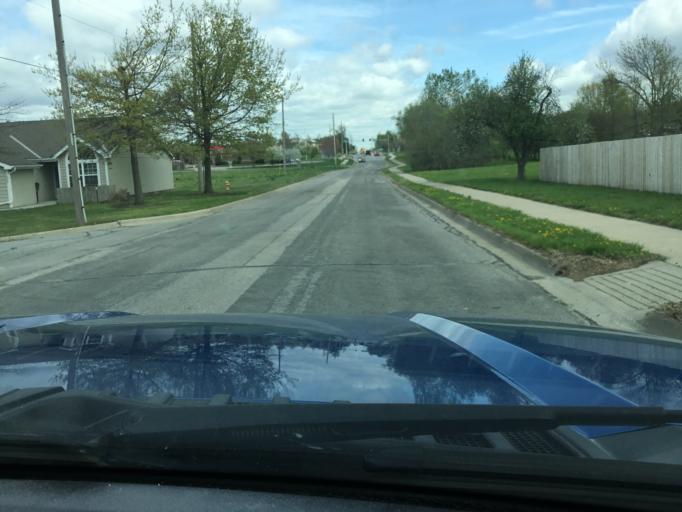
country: US
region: Kansas
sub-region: Douglas County
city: Lawrence
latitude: 38.9402
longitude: -95.2142
